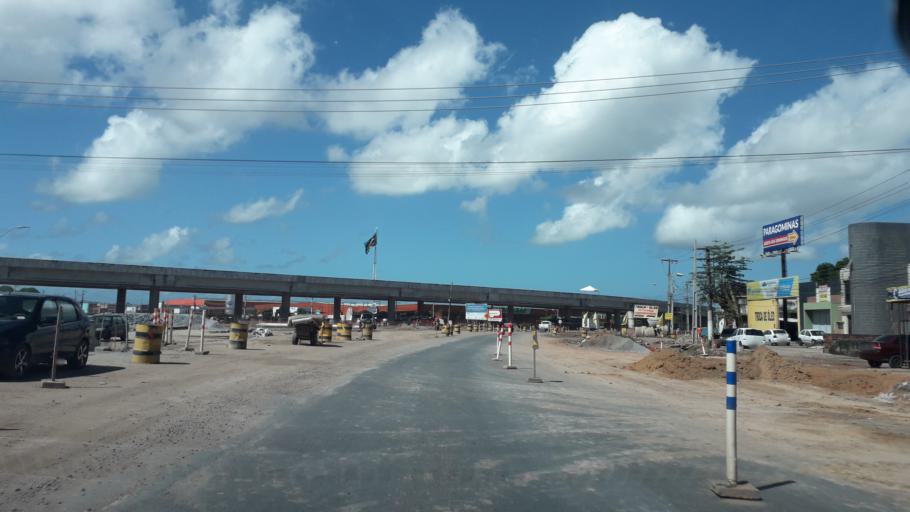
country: BR
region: Alagoas
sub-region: Satuba
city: Satuba
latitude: -9.5661
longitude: -35.7787
